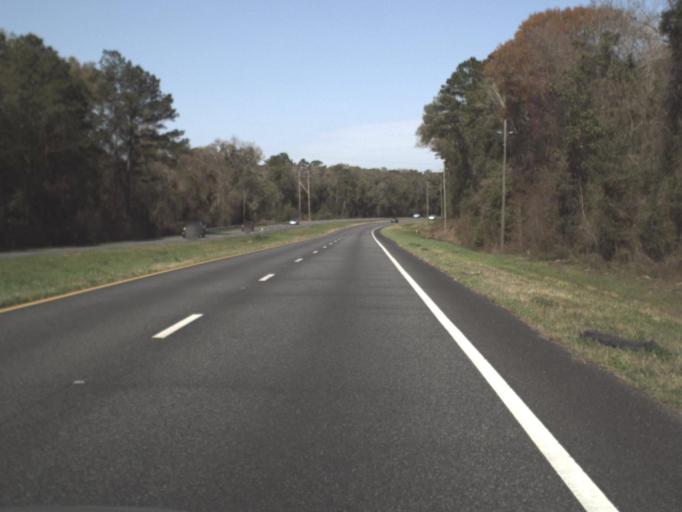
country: US
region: Florida
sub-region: Gadsden County
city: Havana
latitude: 30.5495
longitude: -84.3785
